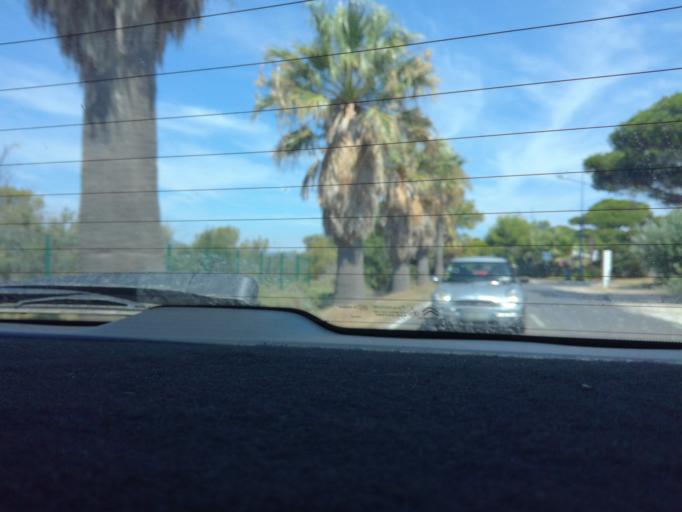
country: FR
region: Provence-Alpes-Cote d'Azur
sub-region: Departement du Var
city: Hyeres
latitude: 43.0504
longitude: 6.1467
